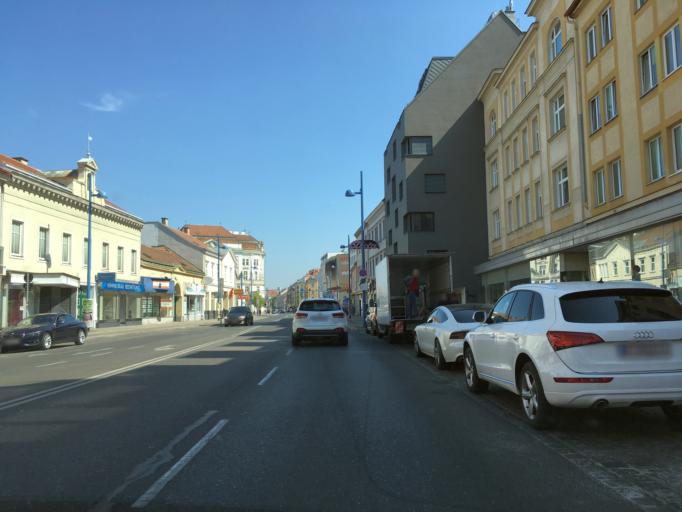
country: AT
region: Vienna
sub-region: Wien Stadt
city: Vienna
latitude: 48.2561
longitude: 16.3966
